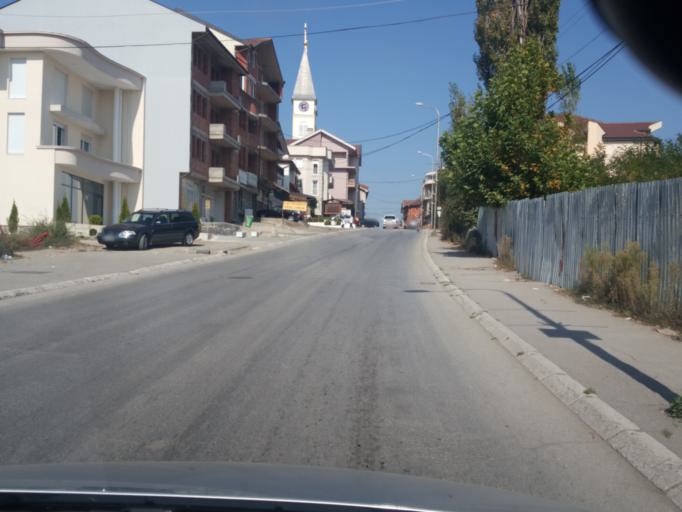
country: XK
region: Gjakova
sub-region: Komuna e Gjakoves
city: Gjakove
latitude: 42.3720
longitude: 20.4228
